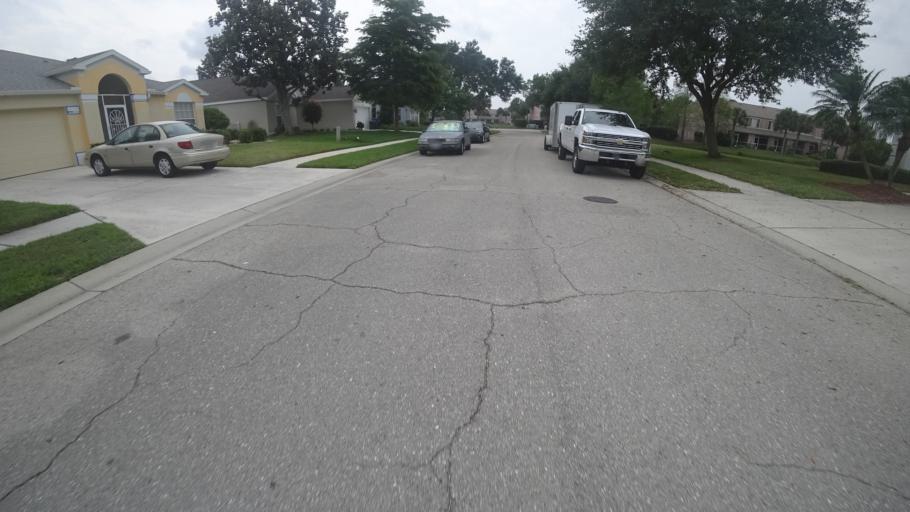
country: US
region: Florida
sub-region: Manatee County
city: Samoset
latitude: 27.4527
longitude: -82.5033
